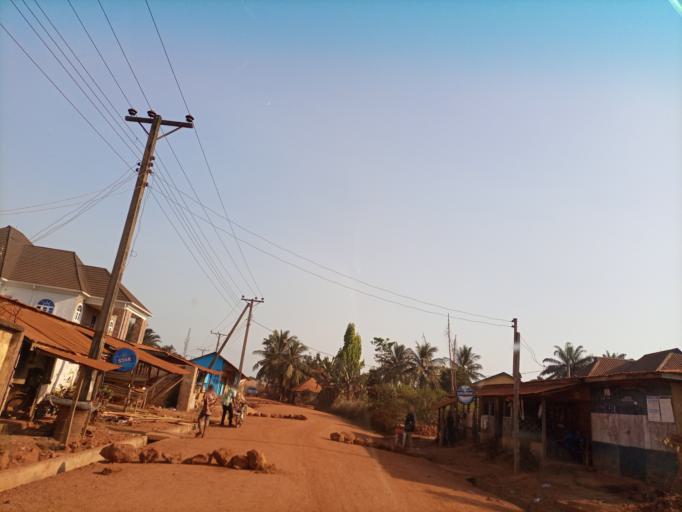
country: NG
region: Enugu
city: Opi
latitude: 6.7489
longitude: 7.4100
